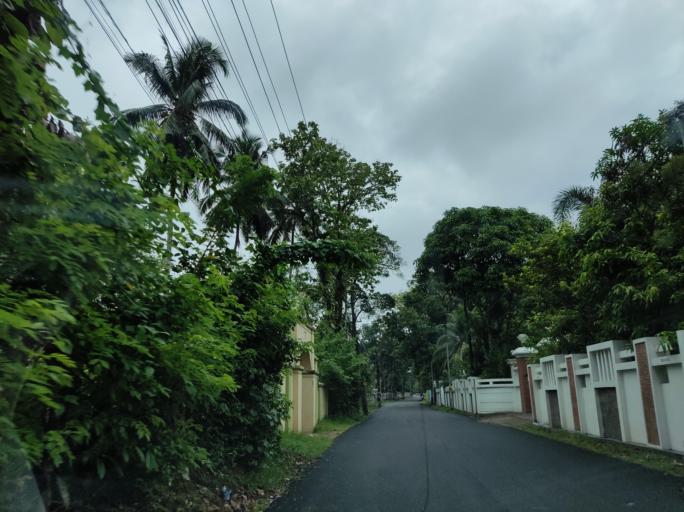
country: IN
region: Kerala
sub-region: Alappuzha
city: Mavelikara
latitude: 9.2481
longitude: 76.5289
